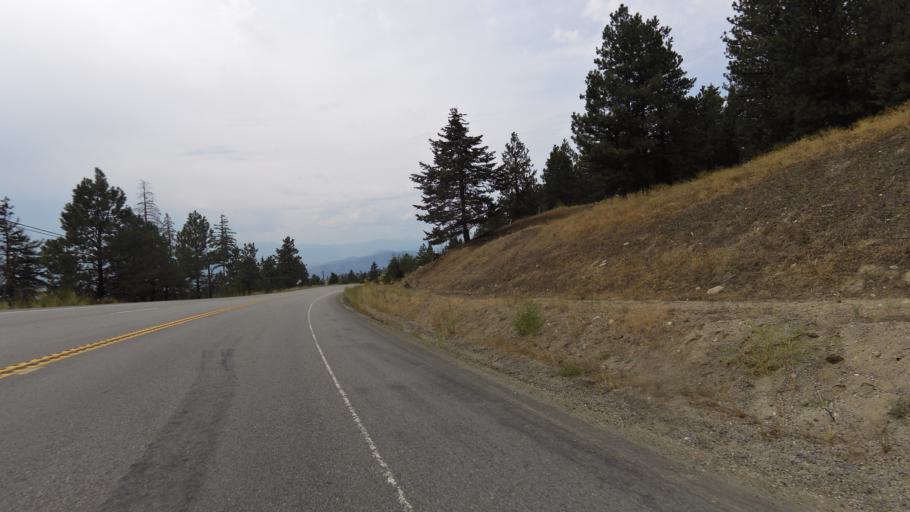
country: CA
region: British Columbia
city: Osoyoos
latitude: 49.0065
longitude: -119.3409
